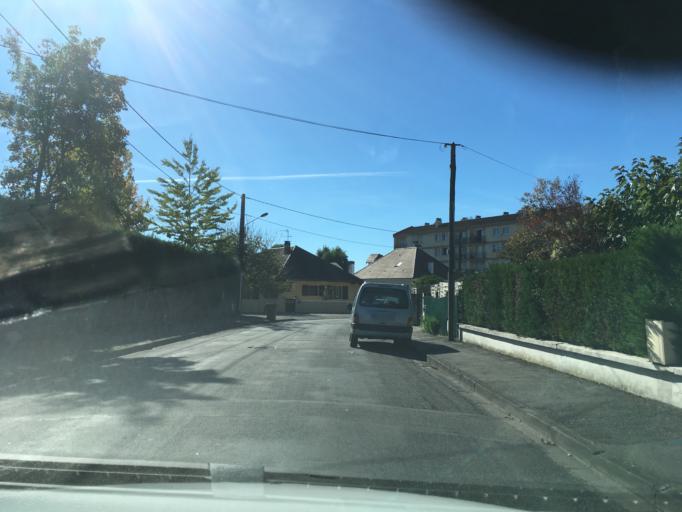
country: FR
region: Aquitaine
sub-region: Departement des Pyrenees-Atlantiques
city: Pau
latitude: 43.3219
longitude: -0.3743
